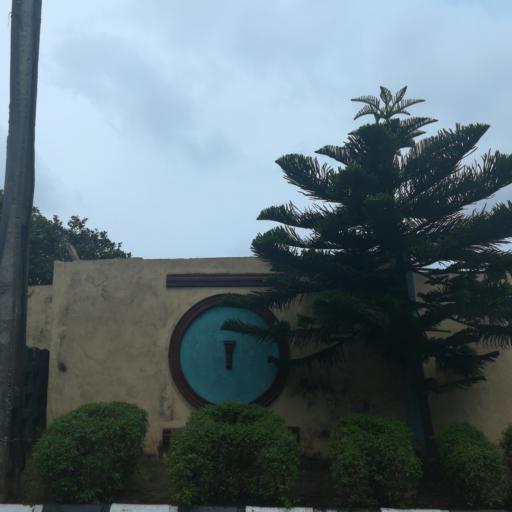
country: NG
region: Lagos
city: Ojota
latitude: 6.5767
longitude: 3.3920
